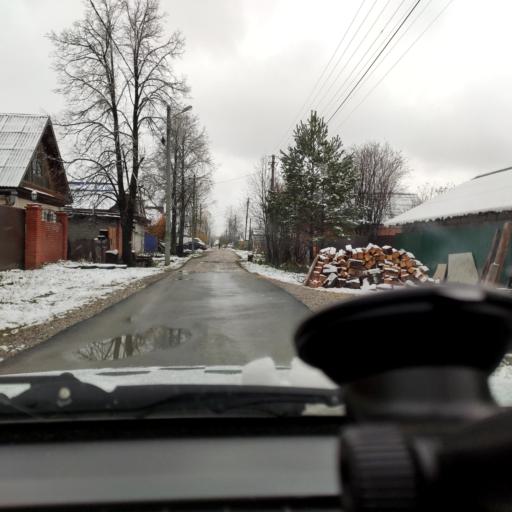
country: RU
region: Perm
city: Perm
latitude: 57.9819
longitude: 56.3078
